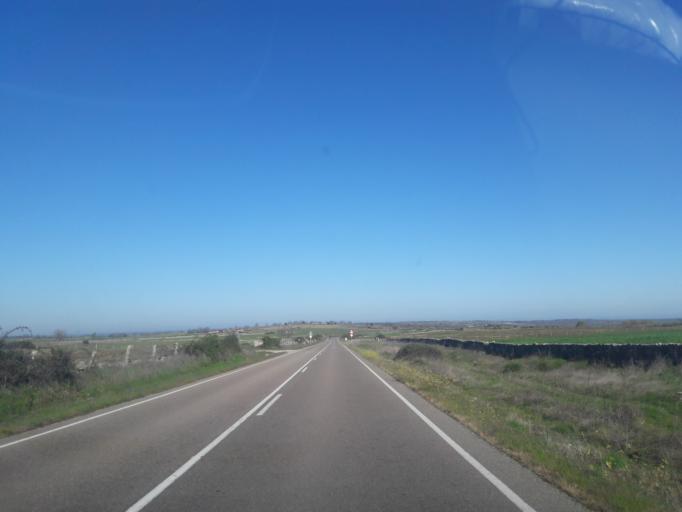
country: ES
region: Castille and Leon
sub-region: Provincia de Salamanca
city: Vitigudino
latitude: 41.0171
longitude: -6.4461
